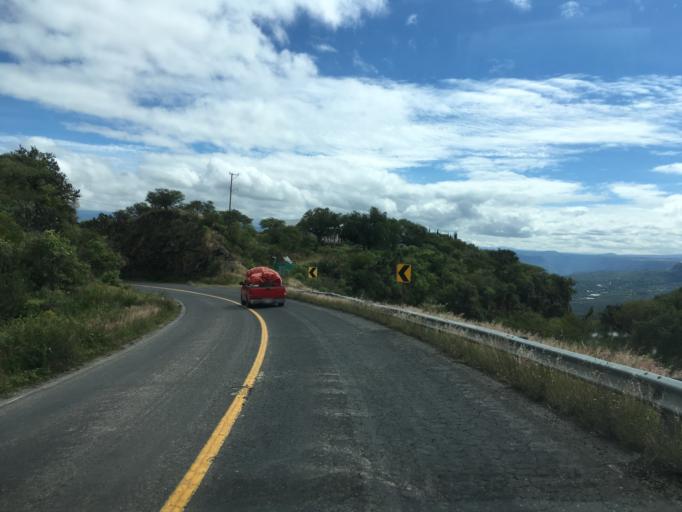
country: MX
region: Hidalgo
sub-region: Atotonilco el Grande
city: Santa Maria Amajac
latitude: 20.4090
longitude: -98.6964
